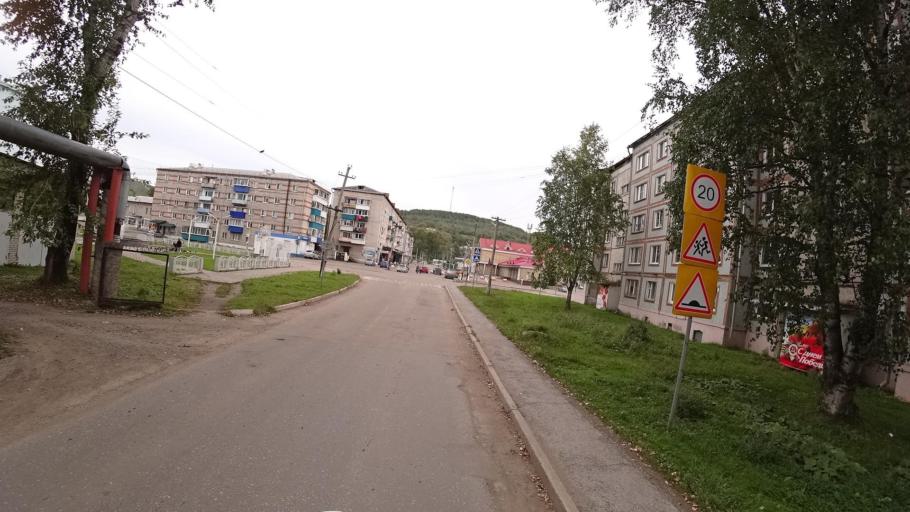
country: RU
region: Jewish Autonomous Oblast
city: Khingansk
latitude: 49.0109
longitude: 131.0535
